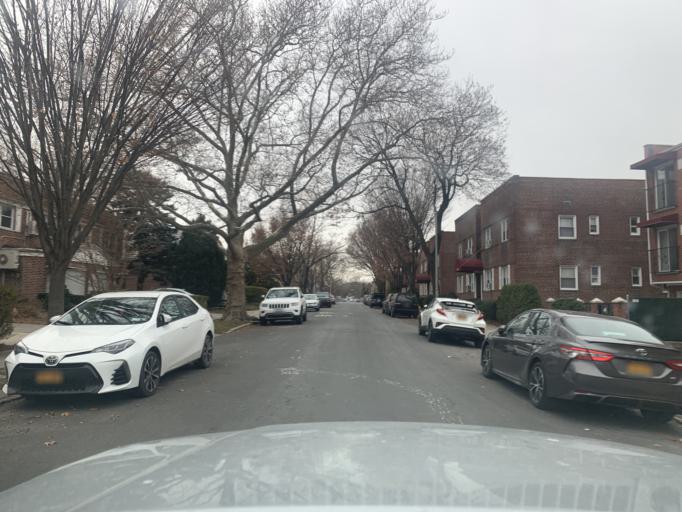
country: US
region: New York
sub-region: Queens County
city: Borough of Queens
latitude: 40.7214
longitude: -73.8669
